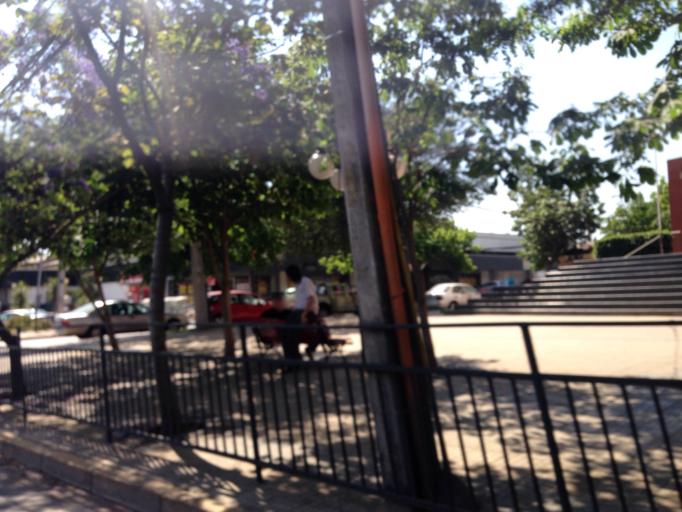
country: CL
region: Santiago Metropolitan
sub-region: Provincia de Santiago
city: Villa Presidente Frei, Nunoa, Santiago, Chile
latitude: -33.4547
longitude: -70.5823
